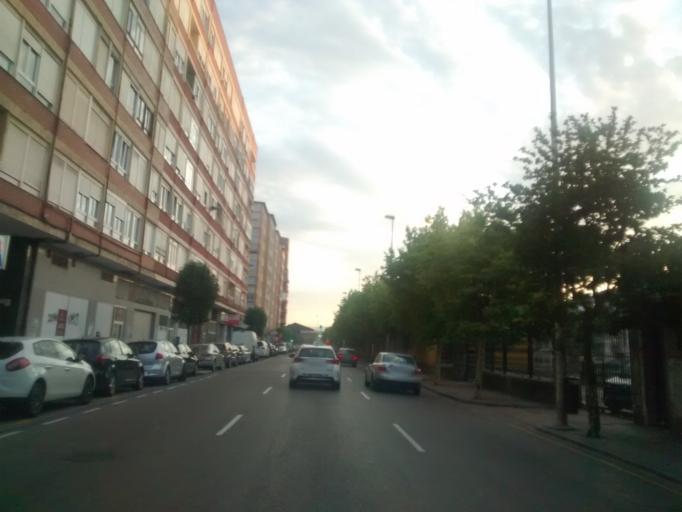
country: ES
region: Cantabria
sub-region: Provincia de Cantabria
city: Santander
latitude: 43.4572
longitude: -3.8137
